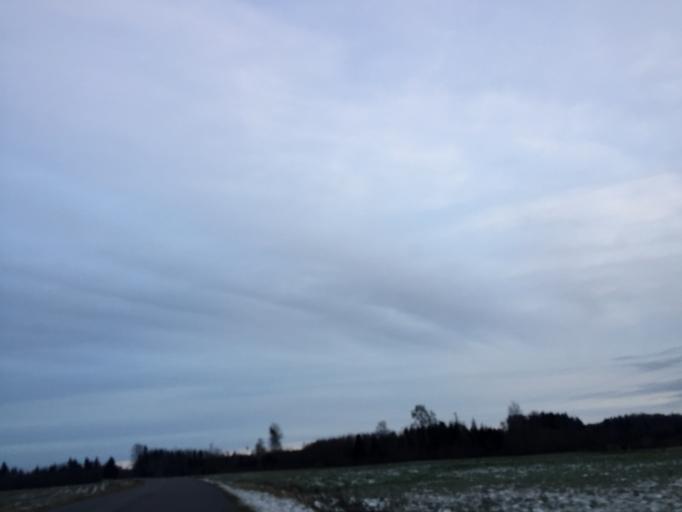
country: LV
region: Aloja
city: Aloja
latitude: 57.6523
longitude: 24.9782
